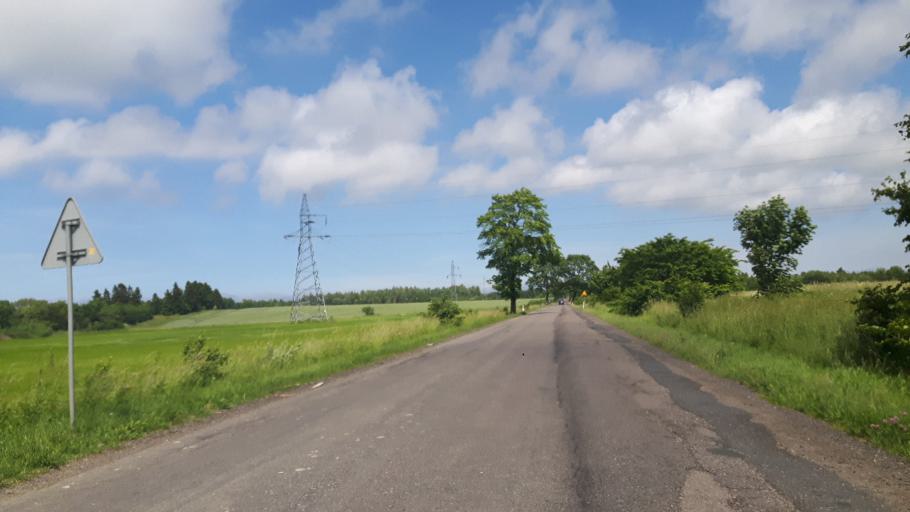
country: PL
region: Pomeranian Voivodeship
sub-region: Powiat slupski
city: Ustka
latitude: 54.5542
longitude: 16.8380
